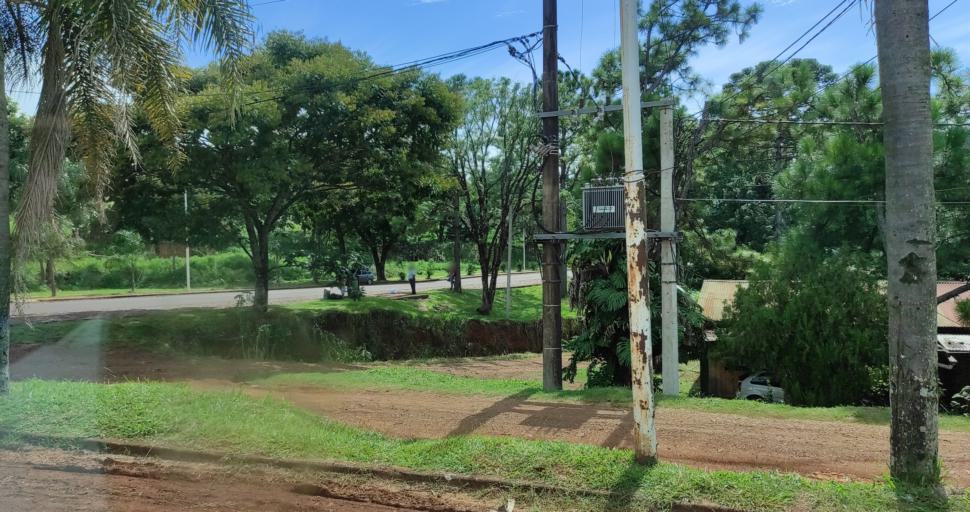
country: AR
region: Misiones
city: Dos de Mayo
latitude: -27.0369
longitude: -54.6848
